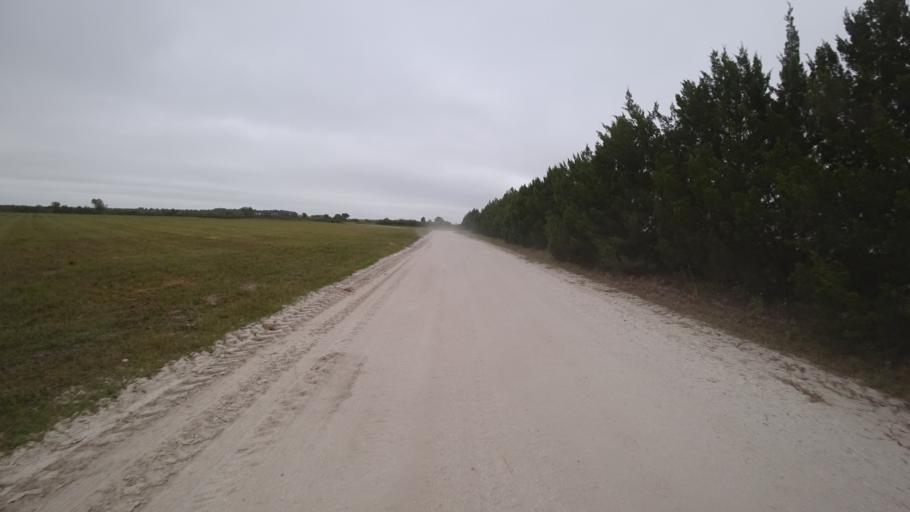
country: US
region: Florida
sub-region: Sarasota County
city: Warm Mineral Springs
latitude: 27.2986
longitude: -82.1346
